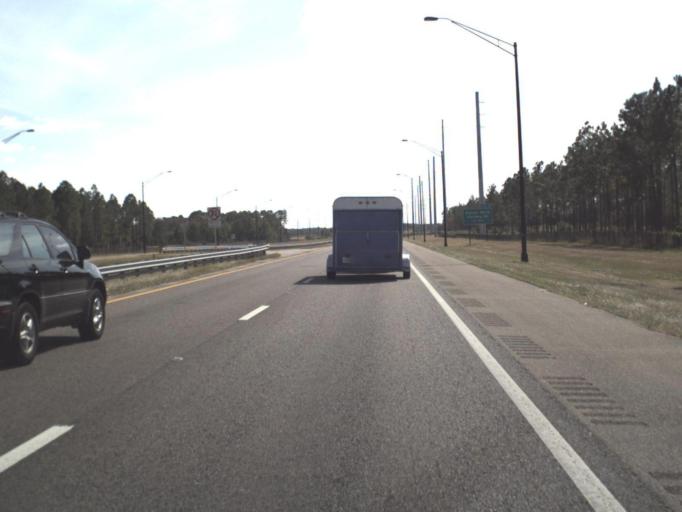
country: US
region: Florida
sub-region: Polk County
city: Citrus Ridge
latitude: 28.3921
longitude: -81.6186
